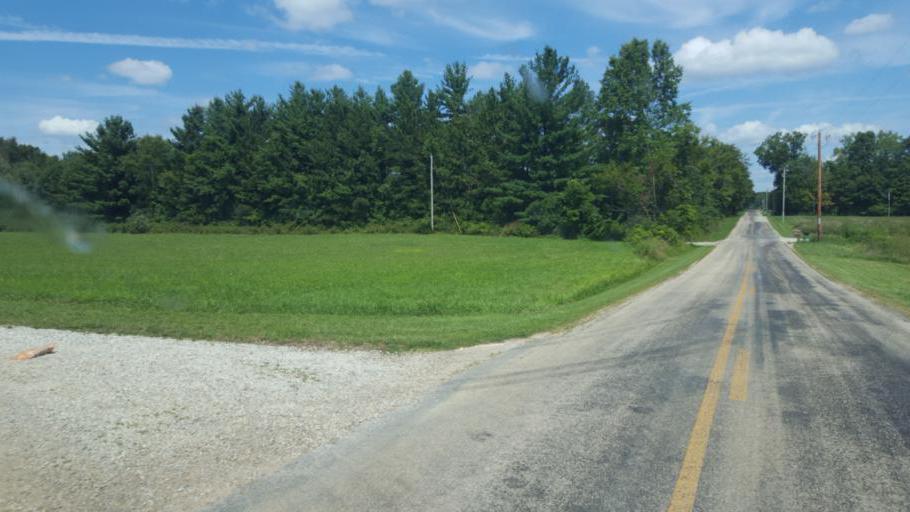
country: US
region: Ohio
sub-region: Delaware County
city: Sunbury
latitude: 40.3325
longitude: -82.8230
